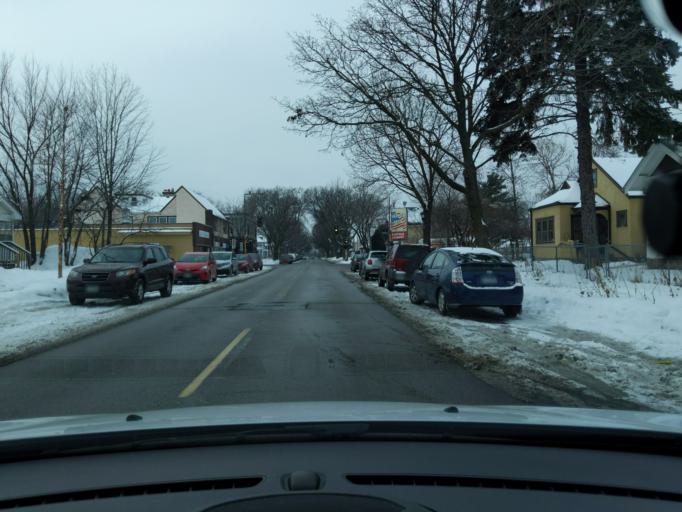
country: US
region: Minnesota
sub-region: Ramsey County
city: Falcon Heights
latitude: 44.9593
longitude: -93.1558
